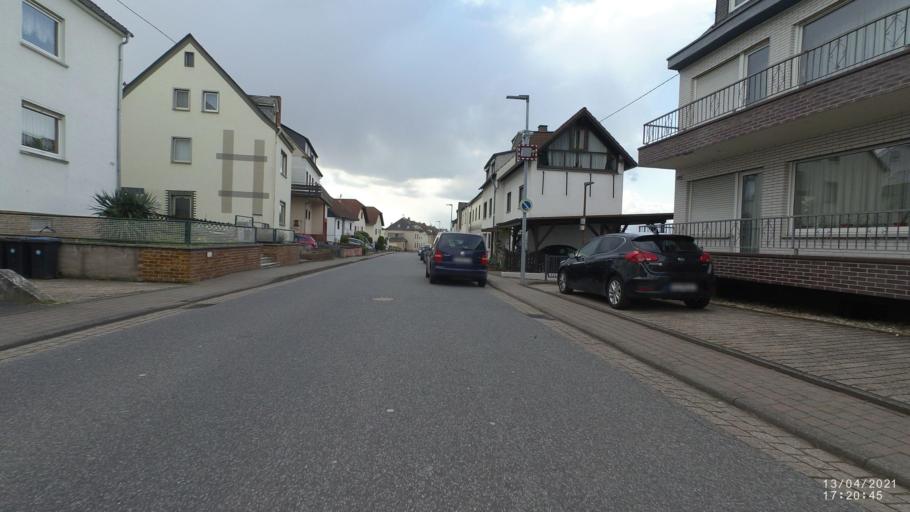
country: DE
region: Rheinland-Pfalz
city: Mulheim-Karlich
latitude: 50.3858
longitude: 7.5102
